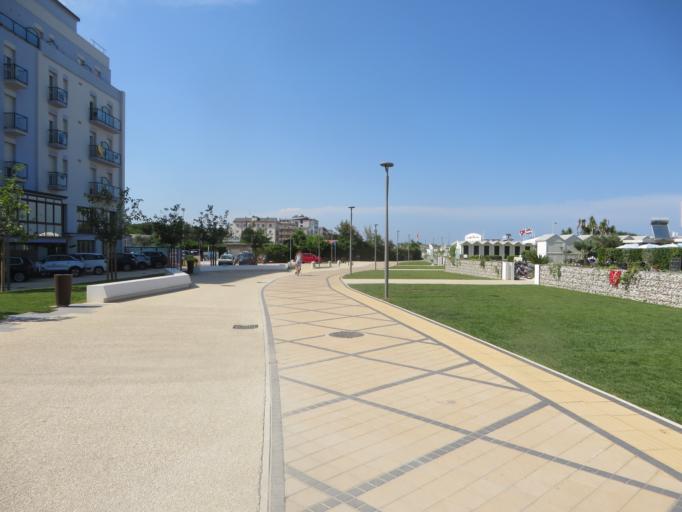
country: IT
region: Emilia-Romagna
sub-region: Provincia di Ravenna
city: Cervia
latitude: 44.2785
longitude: 12.3526
